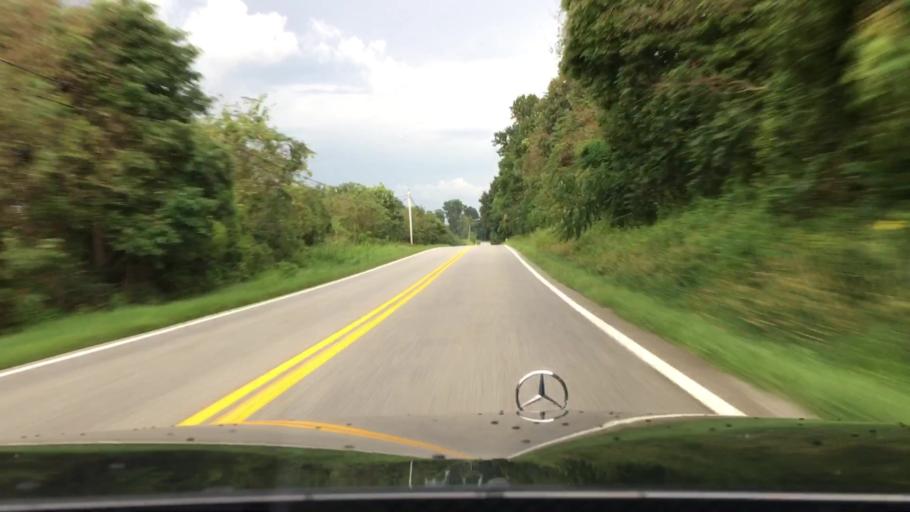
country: US
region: Virginia
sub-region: Nelson County
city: Lovingston
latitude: 37.7820
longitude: -78.9788
